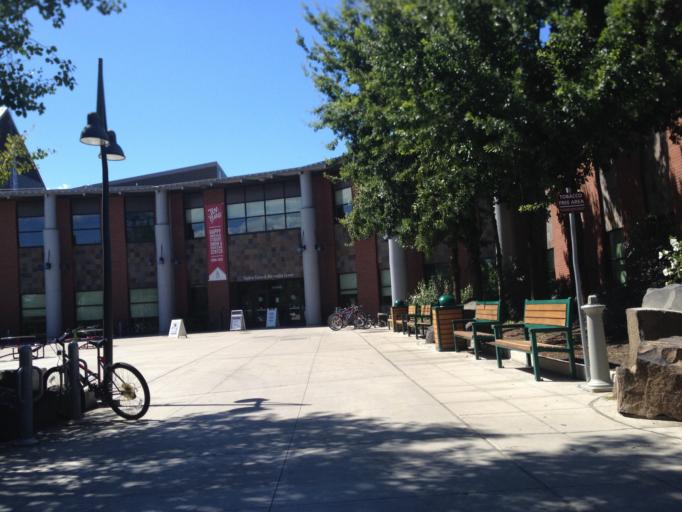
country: US
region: Washington
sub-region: Kittitas County
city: Ellensburg
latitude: 47.0031
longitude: -120.5370
